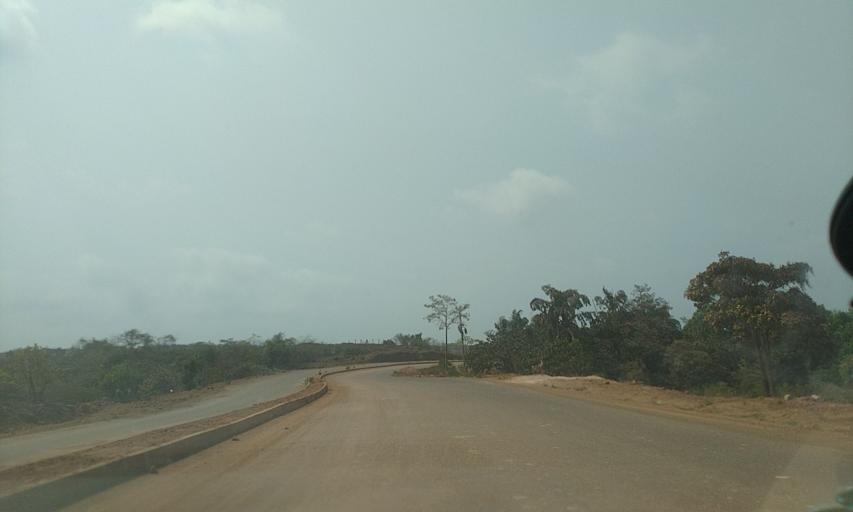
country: IN
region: Goa
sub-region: North Goa
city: Queula
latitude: 15.3511
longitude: 73.9656
